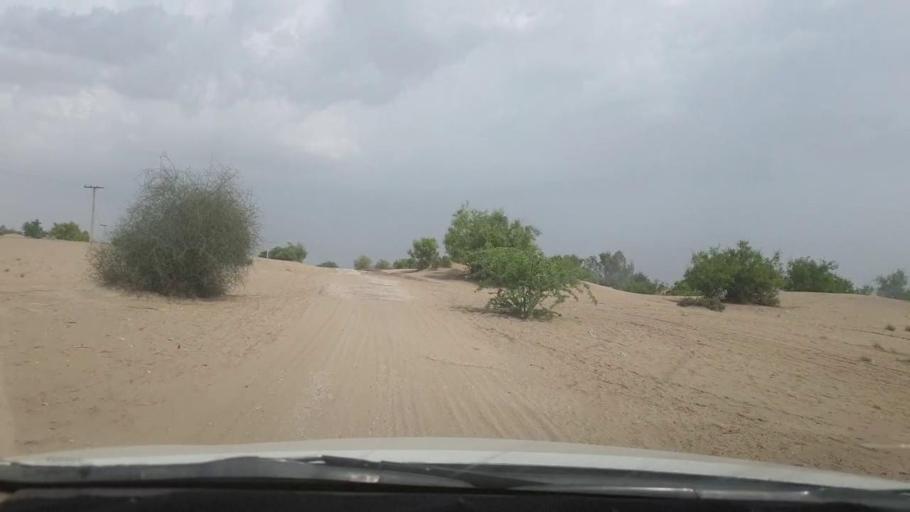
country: PK
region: Sindh
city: Kot Diji
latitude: 27.3383
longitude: 69.0277
